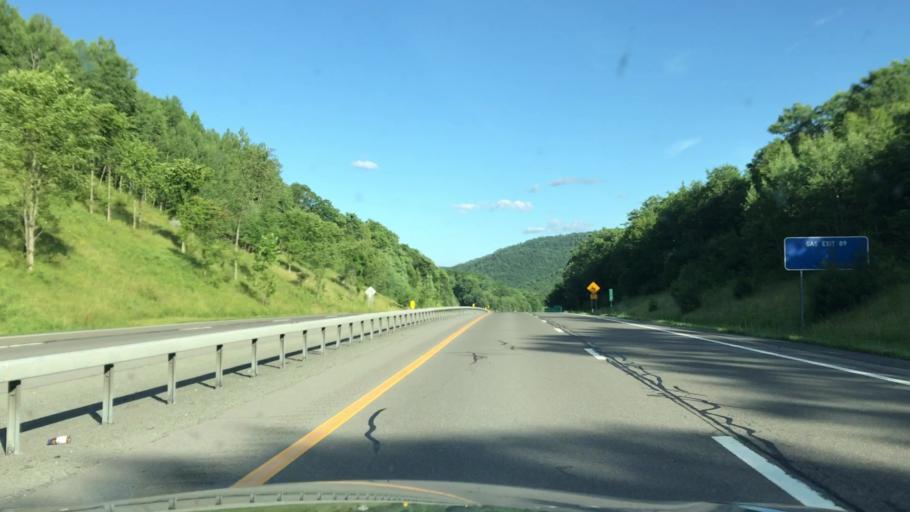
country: US
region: New York
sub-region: Delaware County
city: Hancock
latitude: 41.9733
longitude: -75.1928
